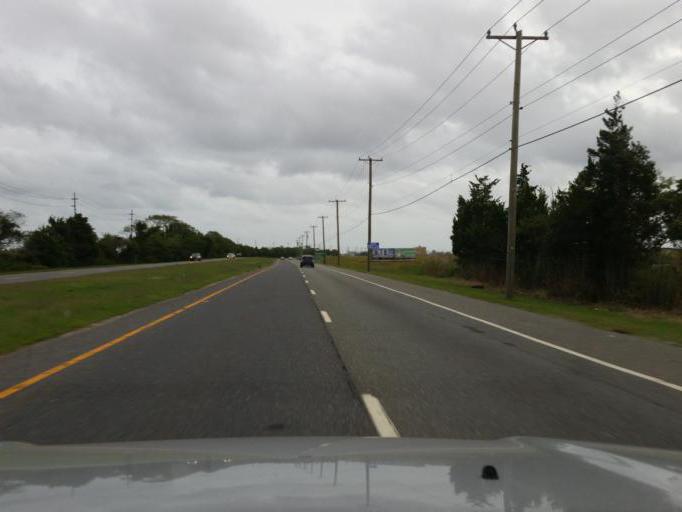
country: US
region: New Jersey
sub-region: Cape May County
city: Rio Grande
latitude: 39.0063
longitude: -74.8621
